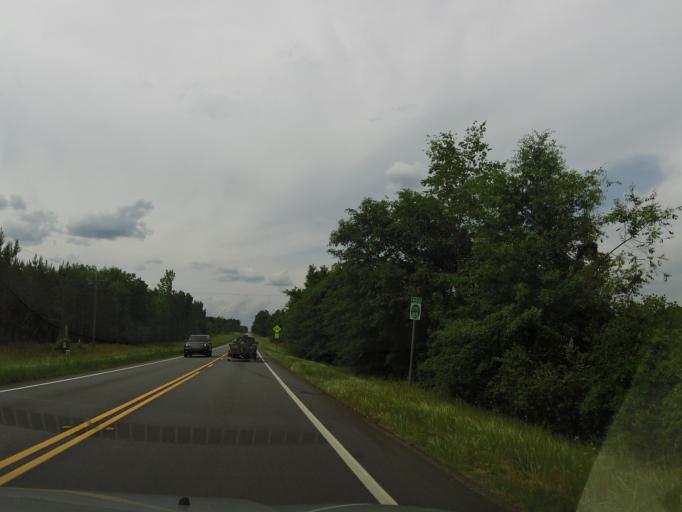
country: US
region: Georgia
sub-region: McDuffie County
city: Thomson
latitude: 33.3721
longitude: -82.4683
